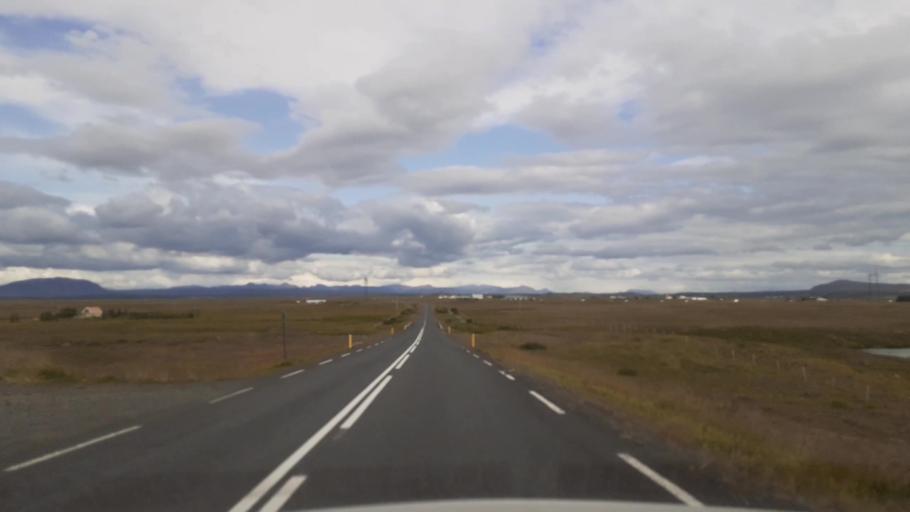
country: IS
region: South
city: Selfoss
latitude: 63.9337
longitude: -20.8418
